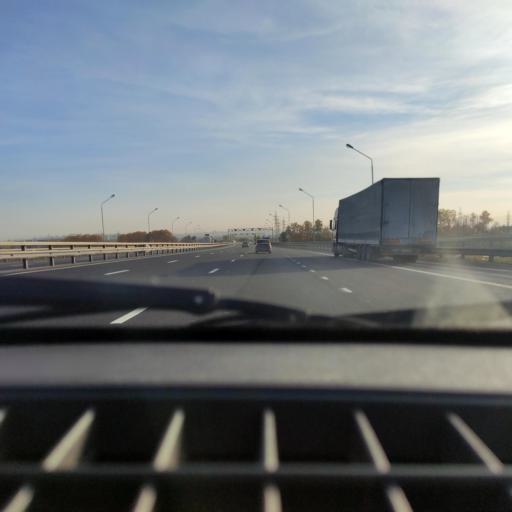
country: RU
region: Bashkortostan
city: Avdon
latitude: 54.6750
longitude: 55.7905
